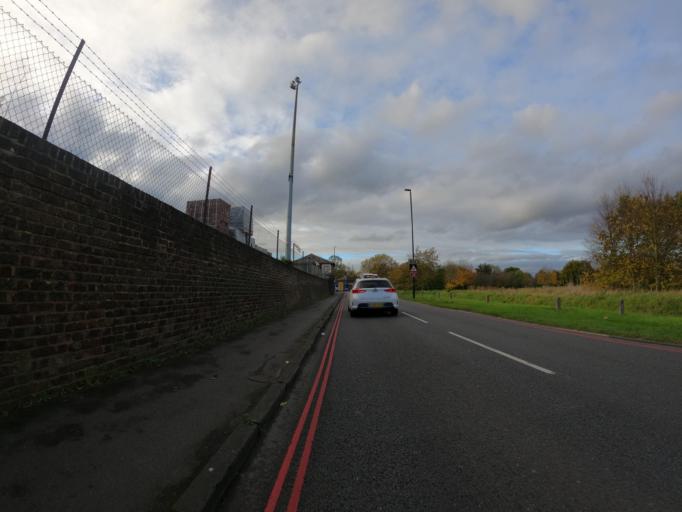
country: GB
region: England
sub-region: Greater London
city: Isleworth
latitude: 51.4885
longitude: -0.3379
